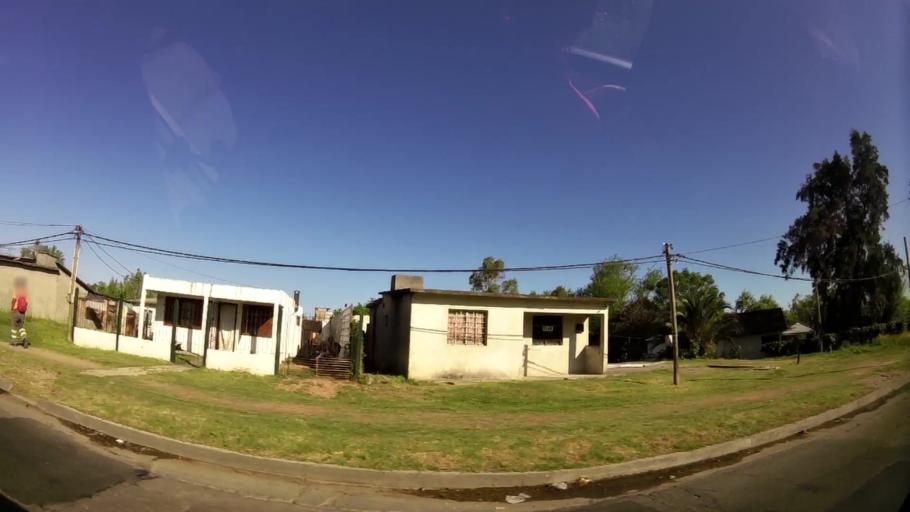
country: UY
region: Montevideo
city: Montevideo
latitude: -34.8273
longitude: -56.1832
